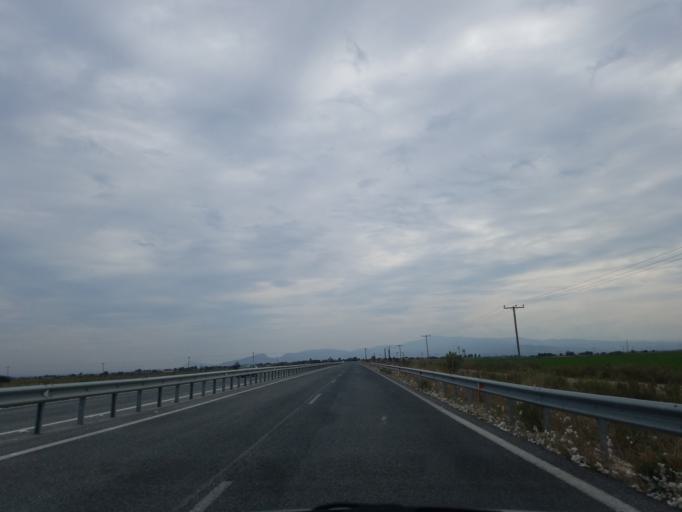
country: GR
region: Thessaly
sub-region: Nomos Kardhitsas
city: Sofades
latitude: 39.2932
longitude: 22.1724
